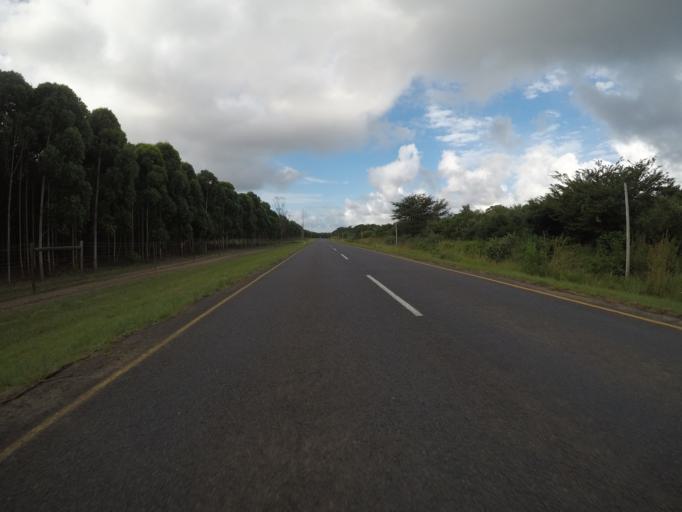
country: ZA
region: KwaZulu-Natal
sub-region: uMkhanyakude District Municipality
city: Mtubatuba
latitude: -28.3749
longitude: 32.2521
